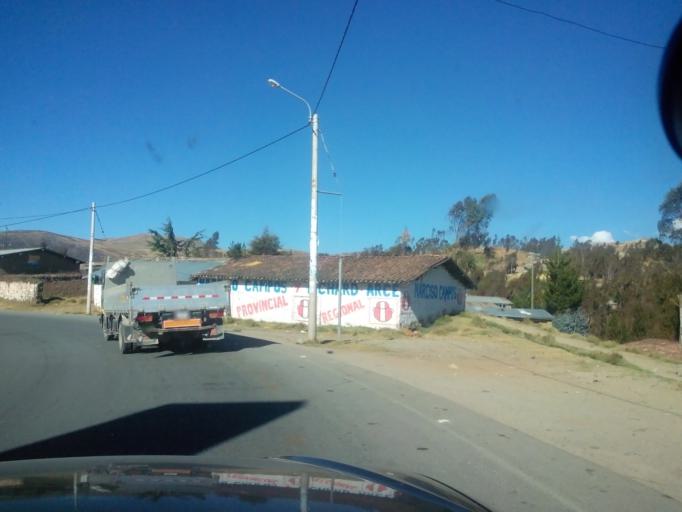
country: PE
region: Apurimac
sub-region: Provincia de Andahuaylas
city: Pacucha
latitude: -13.6512
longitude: -73.3026
